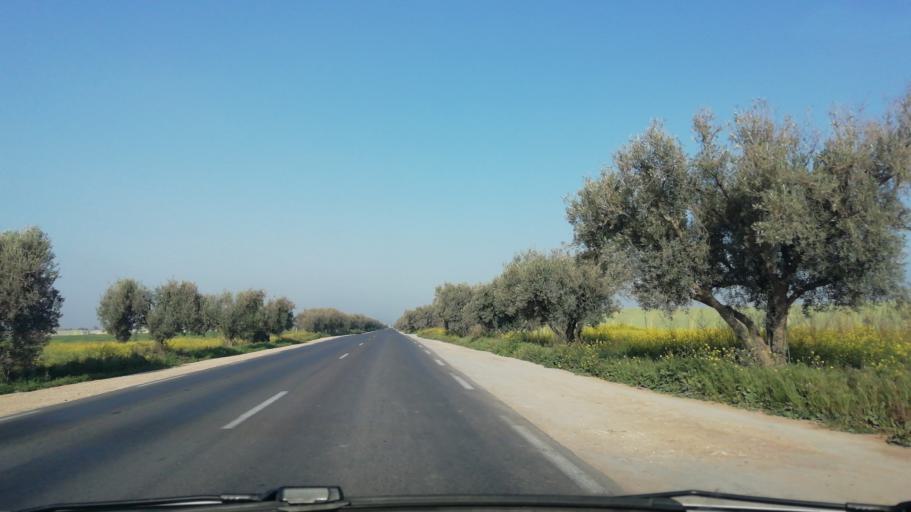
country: DZ
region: Mostaganem
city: Mostaganem
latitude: 35.7453
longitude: 0.1423
